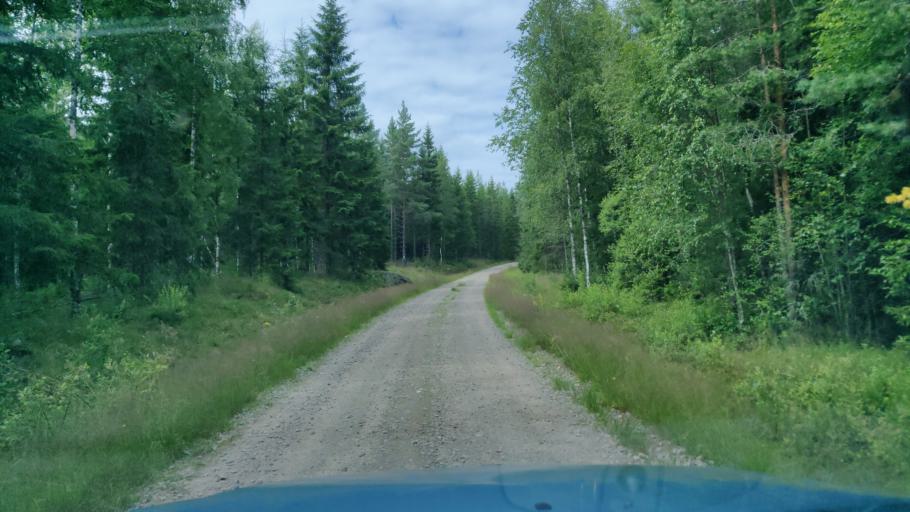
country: SE
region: Vaermland
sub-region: Hagfors Kommun
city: Hagfors
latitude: 59.9415
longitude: 13.5969
